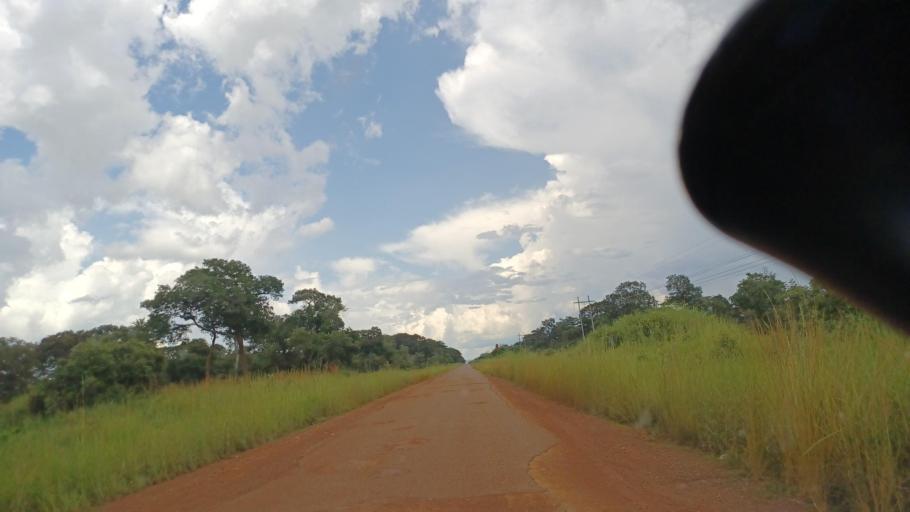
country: ZM
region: North-Western
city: Kasempa
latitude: -12.7968
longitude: 26.0169
